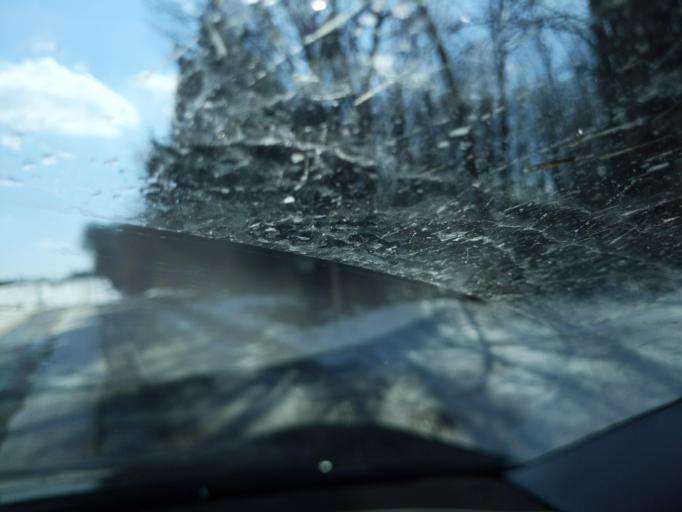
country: US
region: Michigan
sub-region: Livingston County
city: Fowlerville
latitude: 42.5380
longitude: -84.0882
